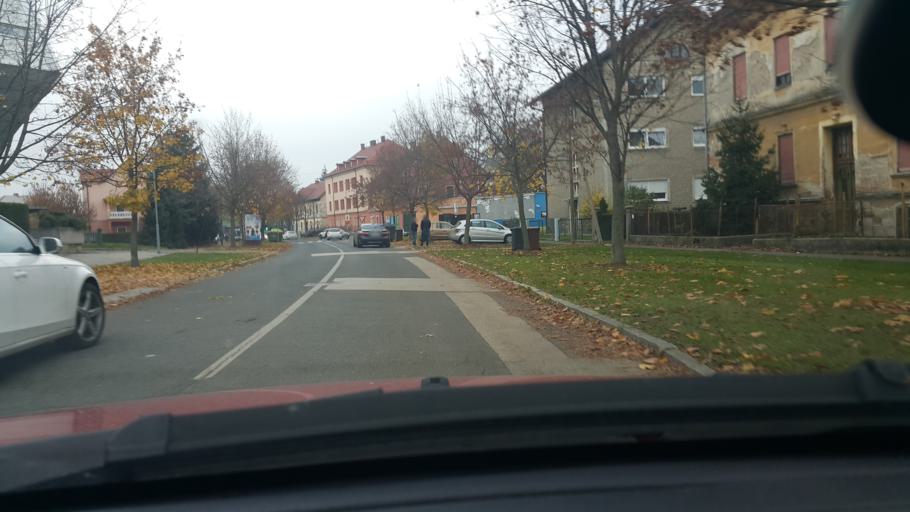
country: SI
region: Maribor
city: Maribor
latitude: 46.5489
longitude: 15.6355
